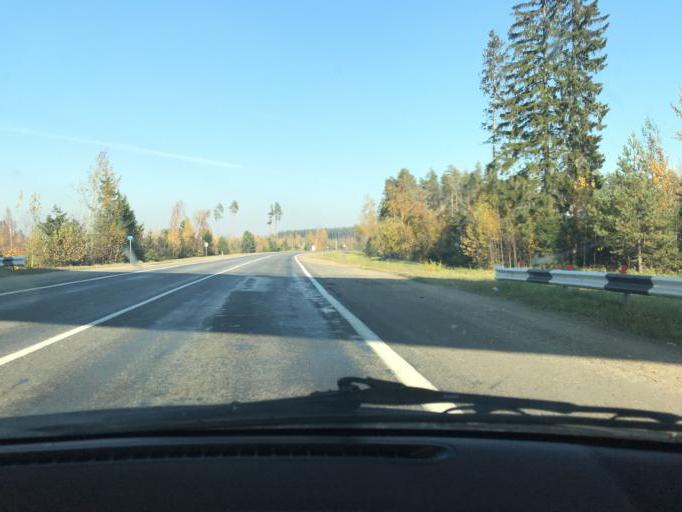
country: BY
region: Vitebsk
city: Orsha
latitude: 54.4040
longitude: 30.4446
